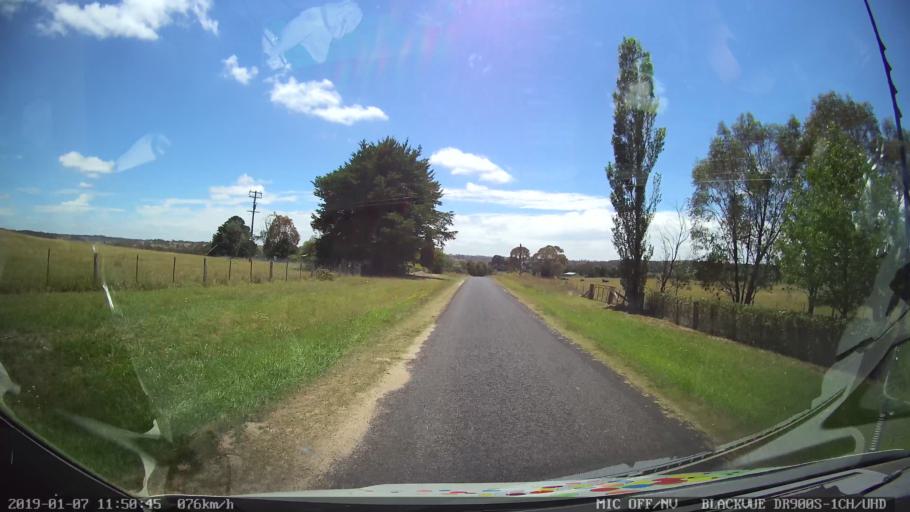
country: AU
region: New South Wales
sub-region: Guyra
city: Guyra
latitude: -30.3112
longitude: 151.6394
